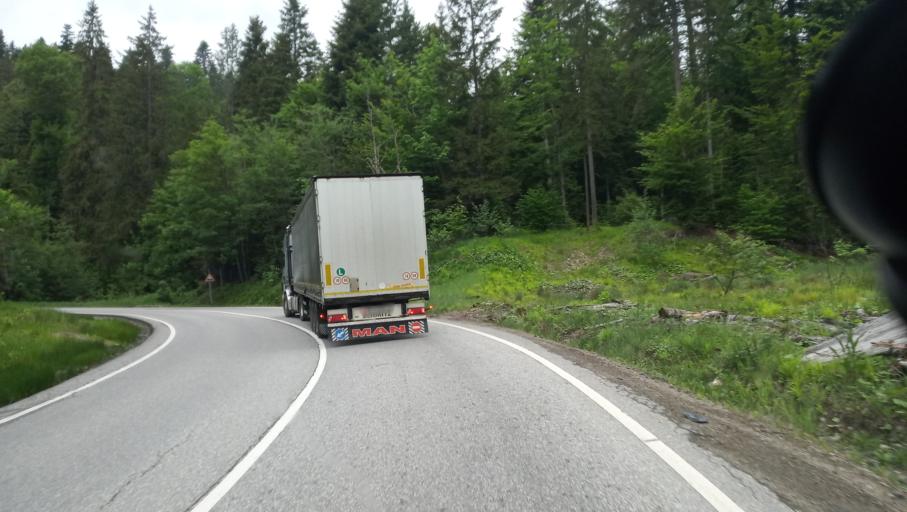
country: RO
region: Neamt
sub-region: Comuna Pipirig
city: Dolhesti
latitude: 47.1663
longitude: 26.0114
